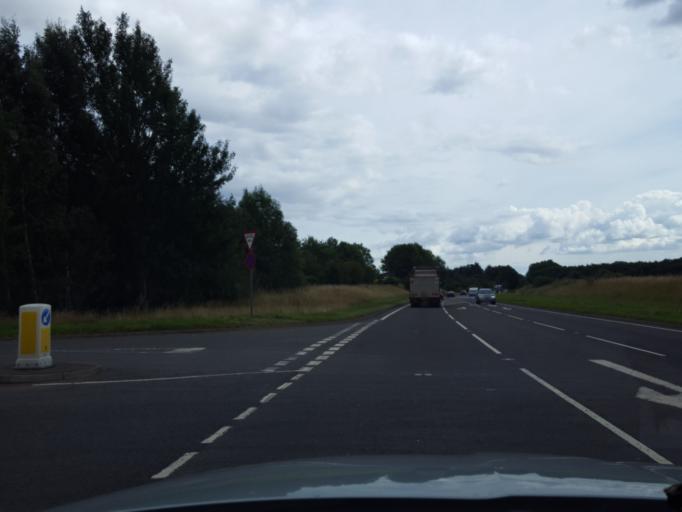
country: GB
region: Scotland
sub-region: Perth and Kinross
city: Luncarty
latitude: 56.4671
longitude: -3.4800
